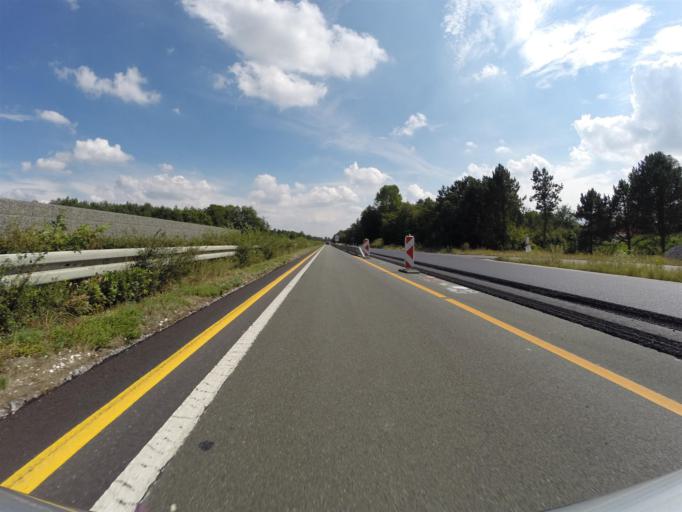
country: DE
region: North Rhine-Westphalia
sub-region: Regierungsbezirk Detmold
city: Hovelhof
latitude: 51.8294
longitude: 8.6964
